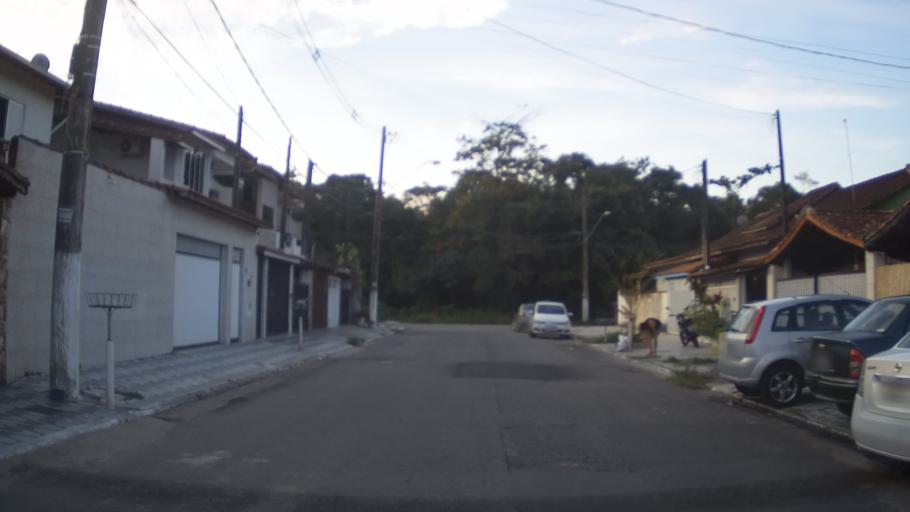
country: BR
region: Sao Paulo
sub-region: Praia Grande
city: Praia Grande
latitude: -23.9923
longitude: -46.4147
